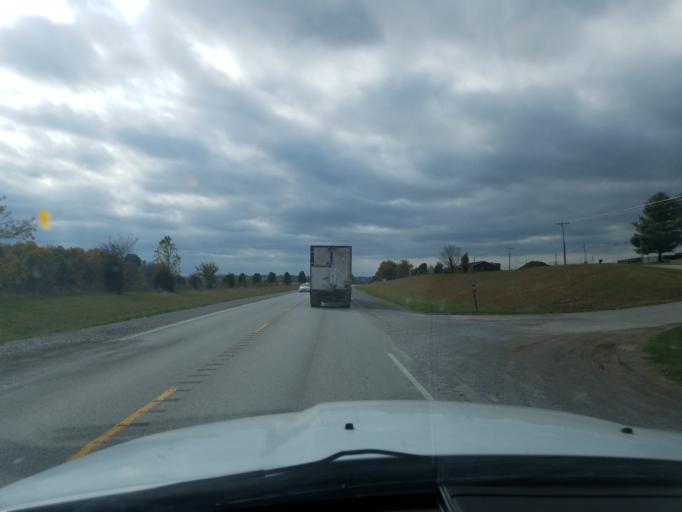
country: US
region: Kentucky
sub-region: Taylor County
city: Campbellsville
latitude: 37.3660
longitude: -85.3090
